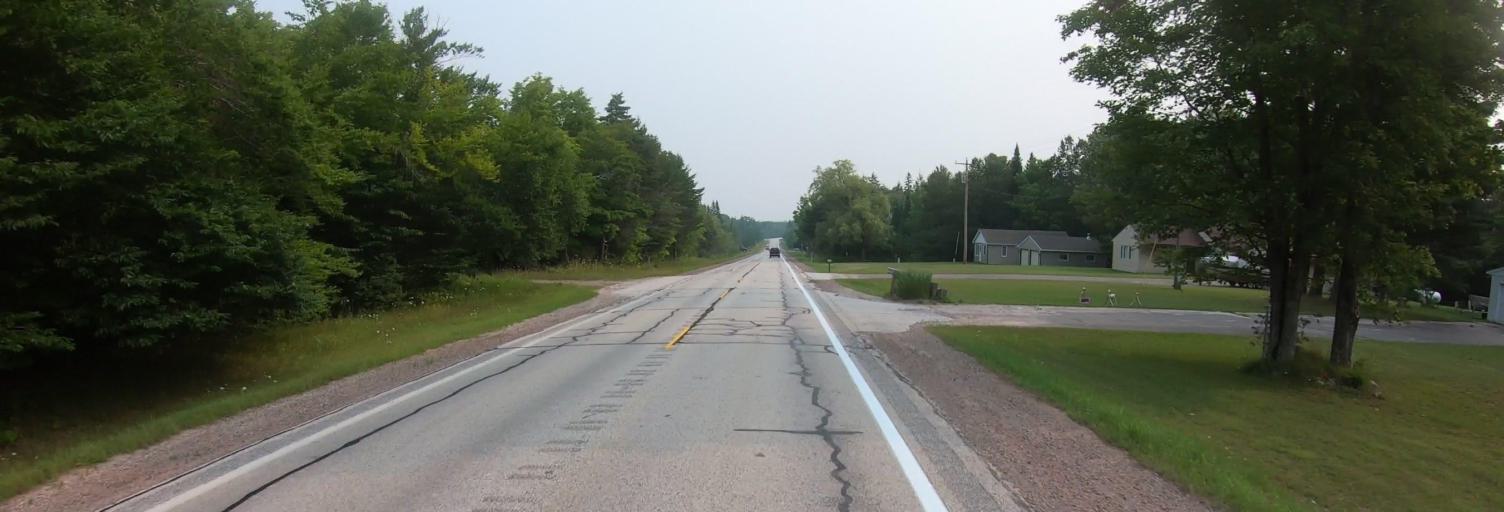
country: US
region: Michigan
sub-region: Luce County
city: Newberry
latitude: 46.5010
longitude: -85.0946
